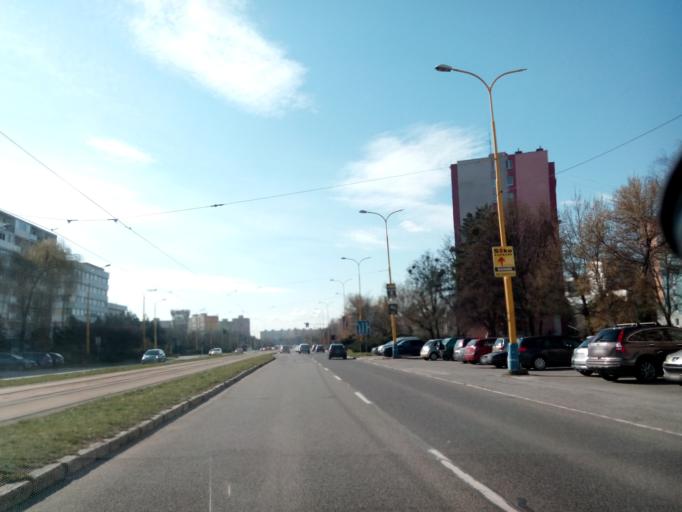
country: SK
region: Kosicky
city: Kosice
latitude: 48.7165
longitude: 21.2343
